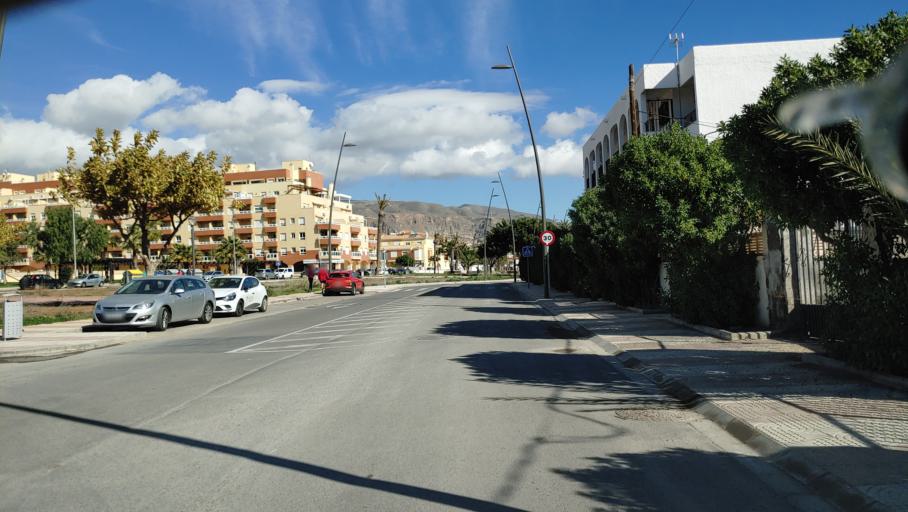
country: ES
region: Andalusia
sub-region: Provincia de Almeria
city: Aguadulce
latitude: 36.7948
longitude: -2.5852
